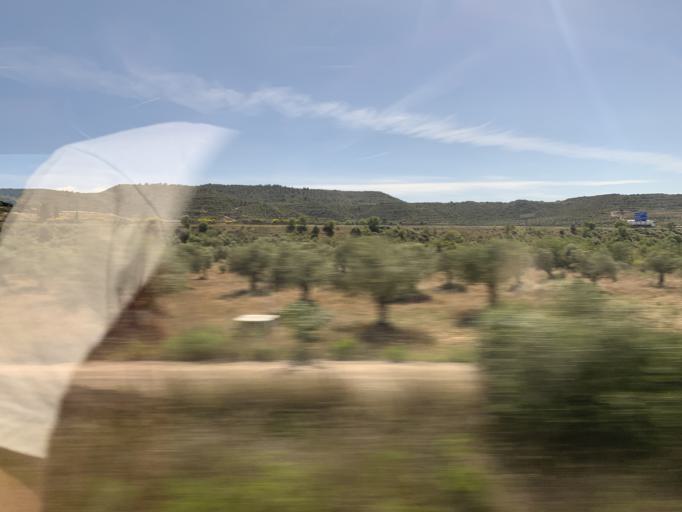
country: ES
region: Catalonia
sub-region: Provincia de Lleida
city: Arbeca
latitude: 41.4794
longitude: 0.8810
